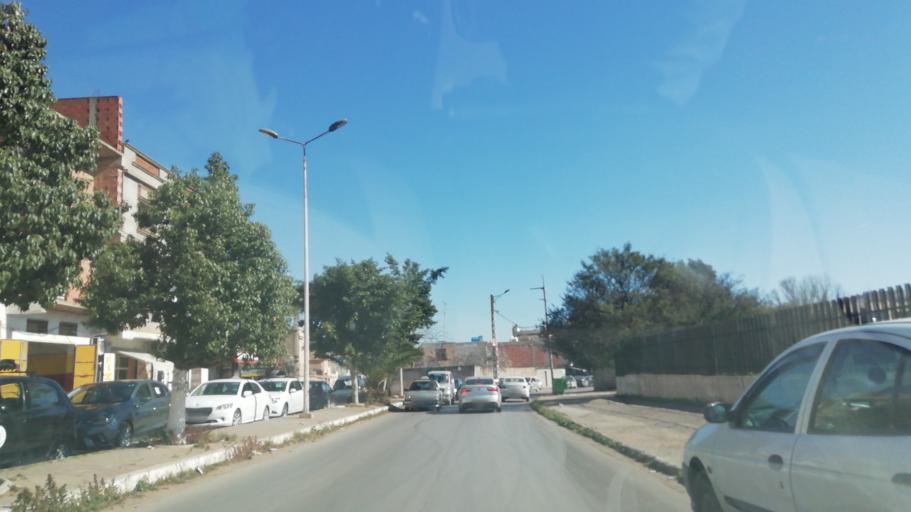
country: DZ
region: Oran
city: Oran
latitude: 35.6717
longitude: -0.6350
